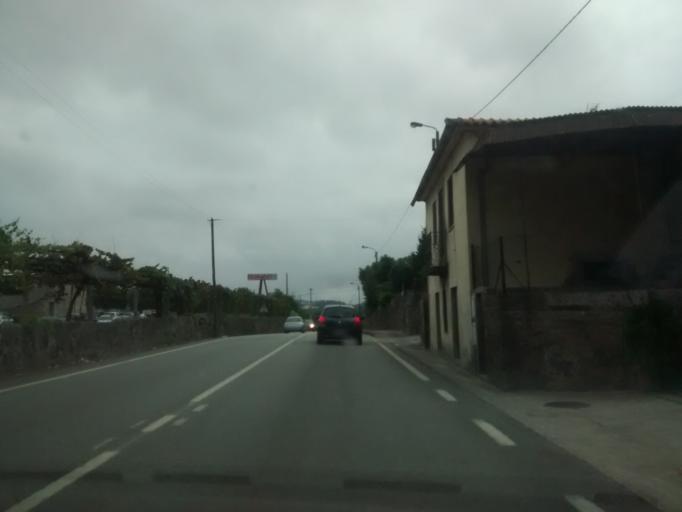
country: PT
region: Braga
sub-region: Braga
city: Oliveira
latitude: 41.4836
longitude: -8.4789
